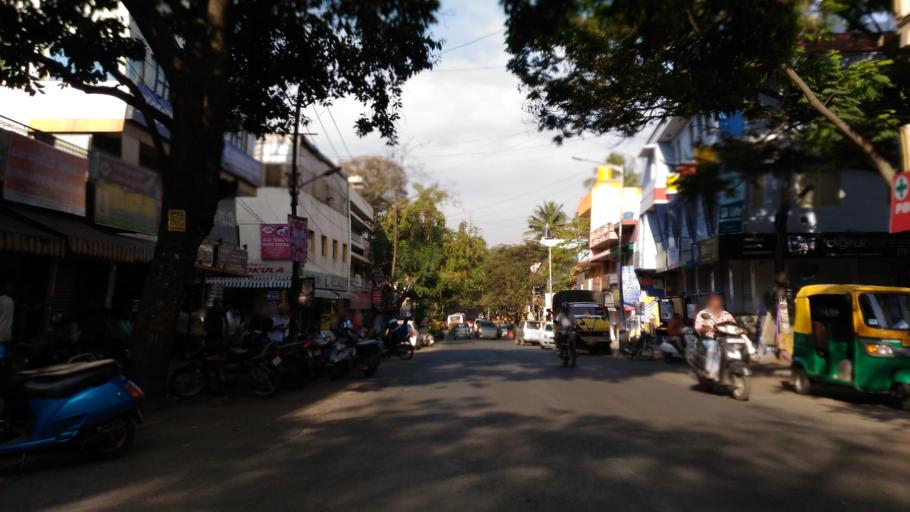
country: IN
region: Karnataka
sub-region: Bangalore Urban
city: Bangalore
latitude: 12.9417
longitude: 77.5568
